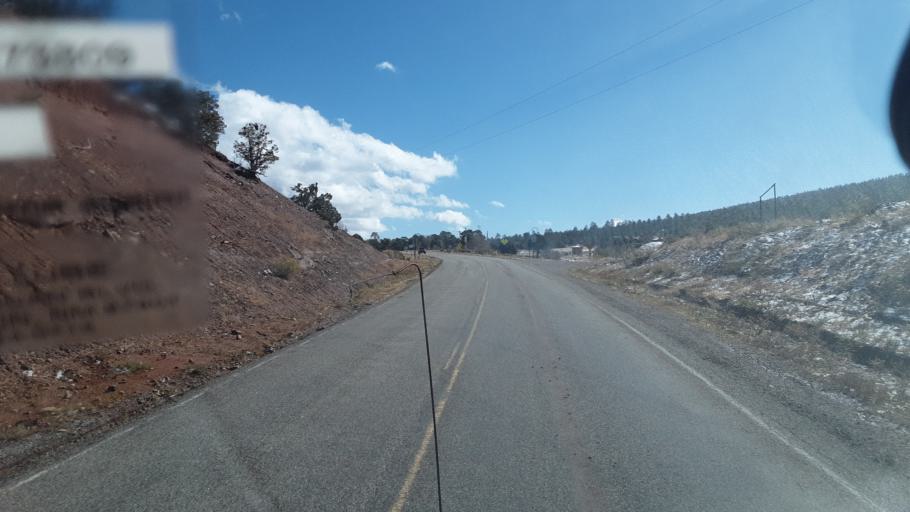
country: US
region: New Mexico
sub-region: Rio Arriba County
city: Santa Teresa
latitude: 36.2297
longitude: -106.8279
